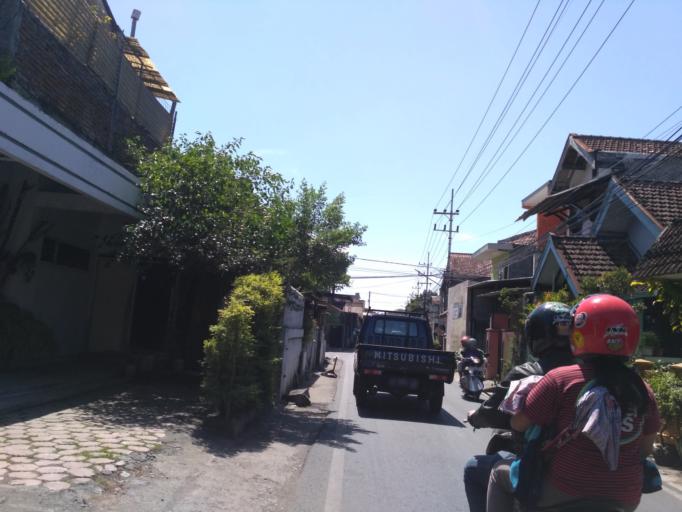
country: ID
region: East Java
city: Malang
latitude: -7.9873
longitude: 112.6453
